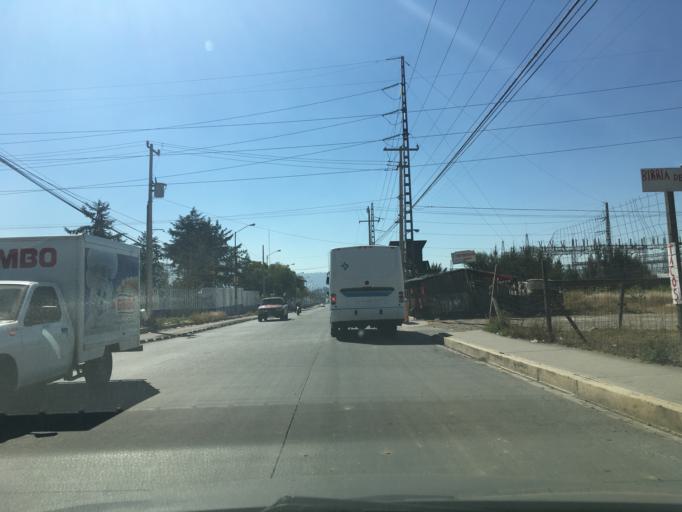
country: MX
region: Michoacan
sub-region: Morelia
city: San Antonio
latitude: 19.6923
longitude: -101.2505
